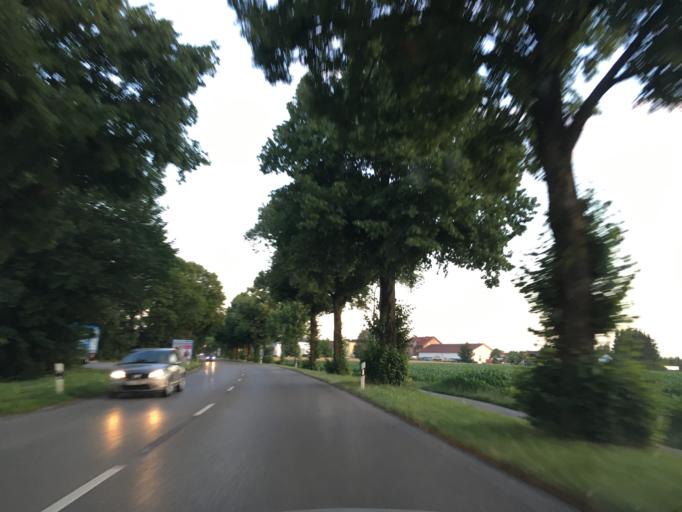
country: DE
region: Bavaria
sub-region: Upper Bavaria
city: Erding
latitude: 48.2911
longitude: 11.8990
